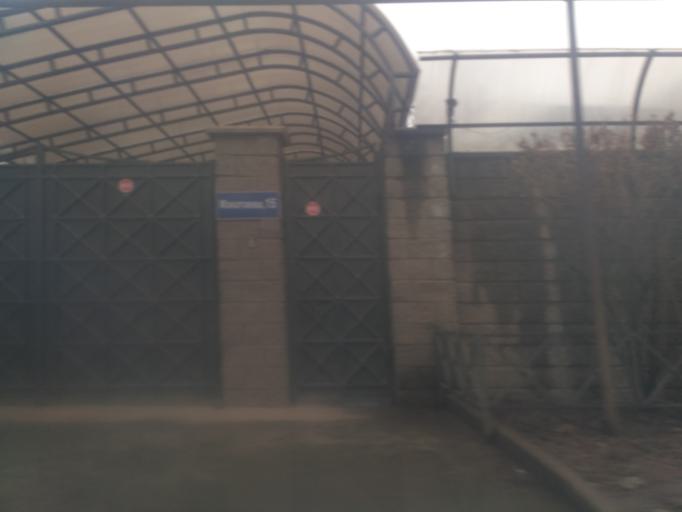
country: KZ
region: Almaty Oblysy
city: Burunday
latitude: 43.2186
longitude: 76.7609
